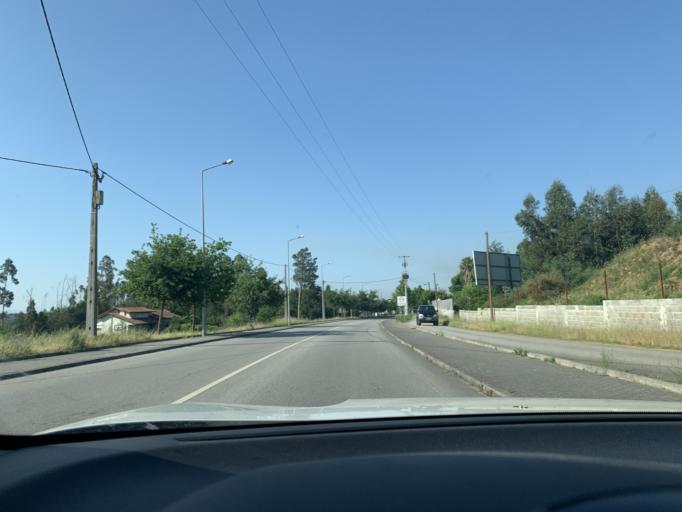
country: PT
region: Viseu
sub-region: Concelho de Tondela
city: Tondela
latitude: 40.4979
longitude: -8.0839
